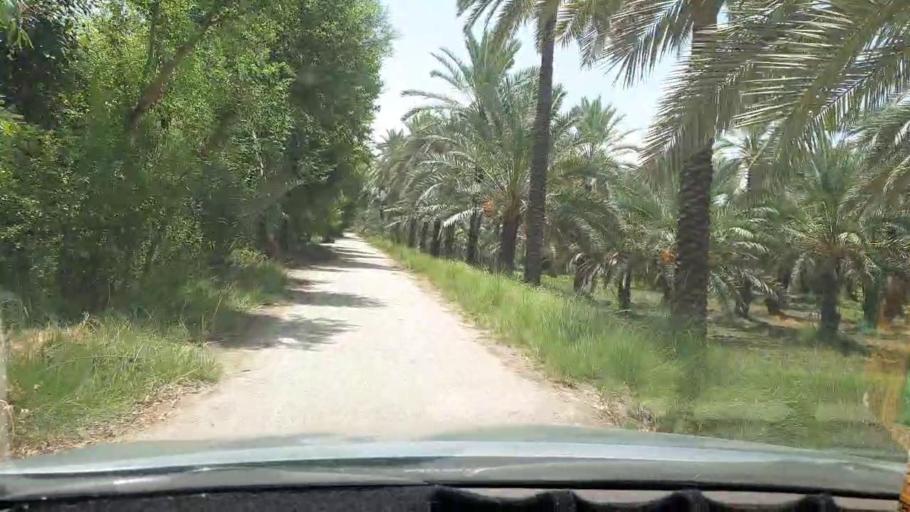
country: PK
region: Sindh
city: Khairpur
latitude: 27.4546
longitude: 68.7816
